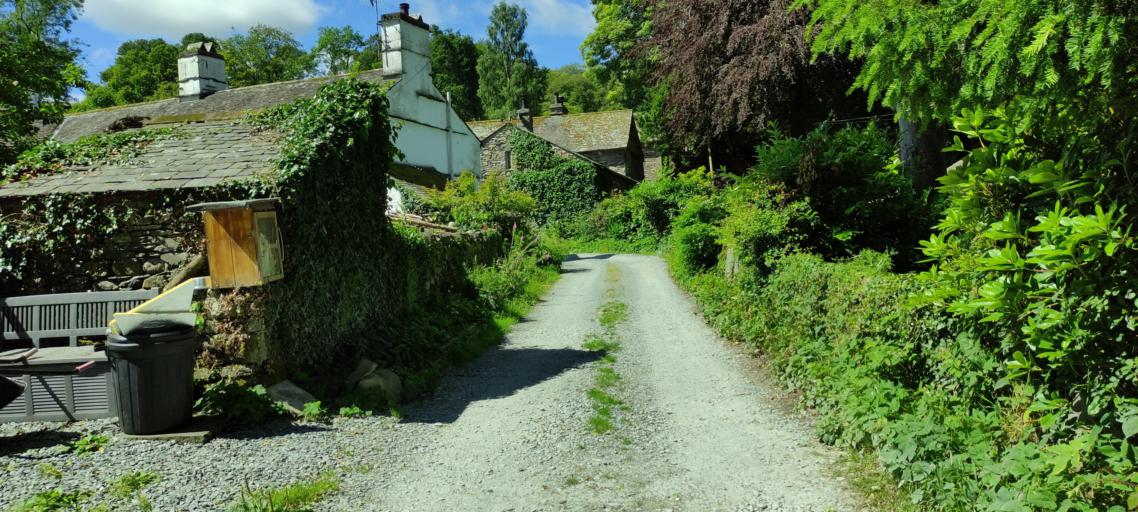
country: GB
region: England
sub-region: Cumbria
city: Ambleside
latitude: 54.3634
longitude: -2.9962
